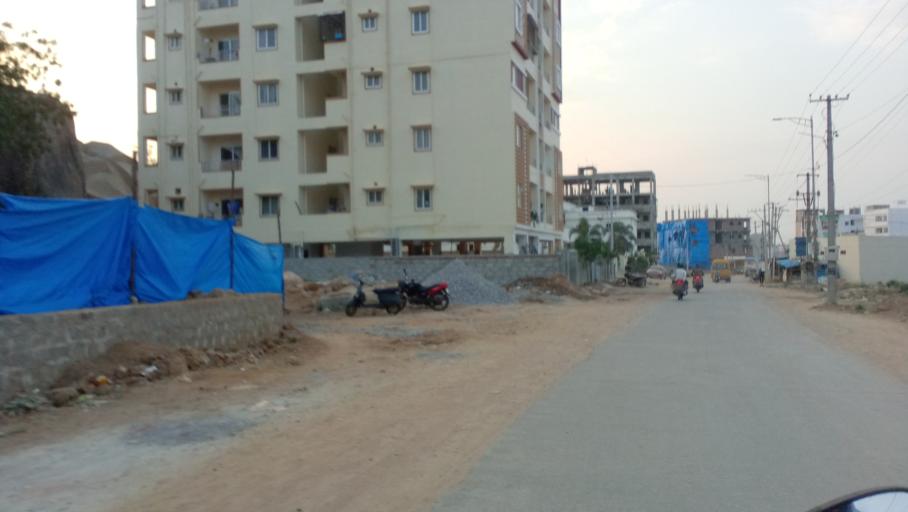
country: IN
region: Telangana
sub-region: Medak
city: Serilingampalle
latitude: 17.5214
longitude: 78.3026
